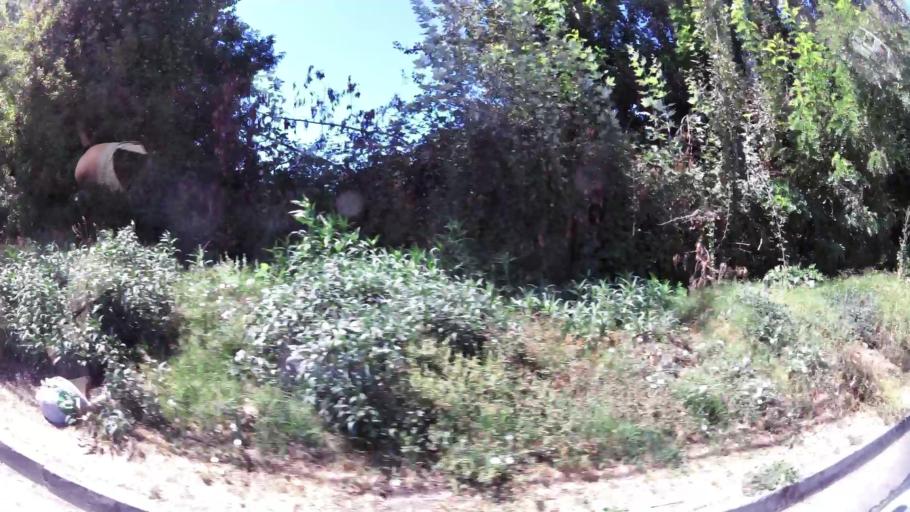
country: CL
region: O'Higgins
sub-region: Provincia de Cachapoal
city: Rancagua
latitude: -34.1516
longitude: -70.7247
